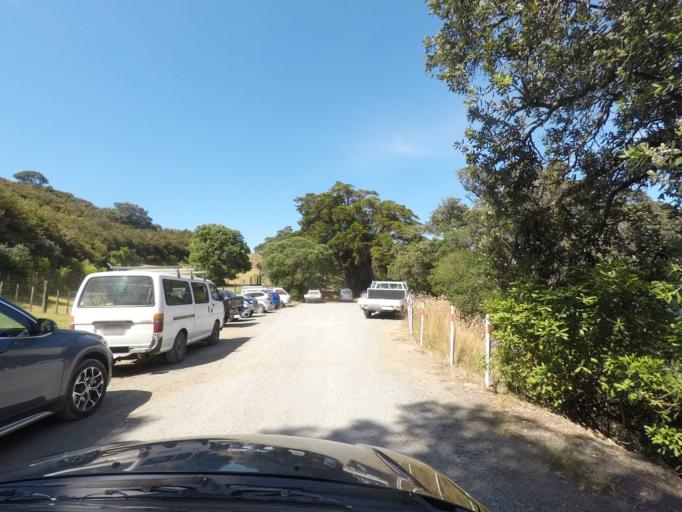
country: NZ
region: Auckland
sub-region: Auckland
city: Warkworth
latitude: -36.3174
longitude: 174.7849
